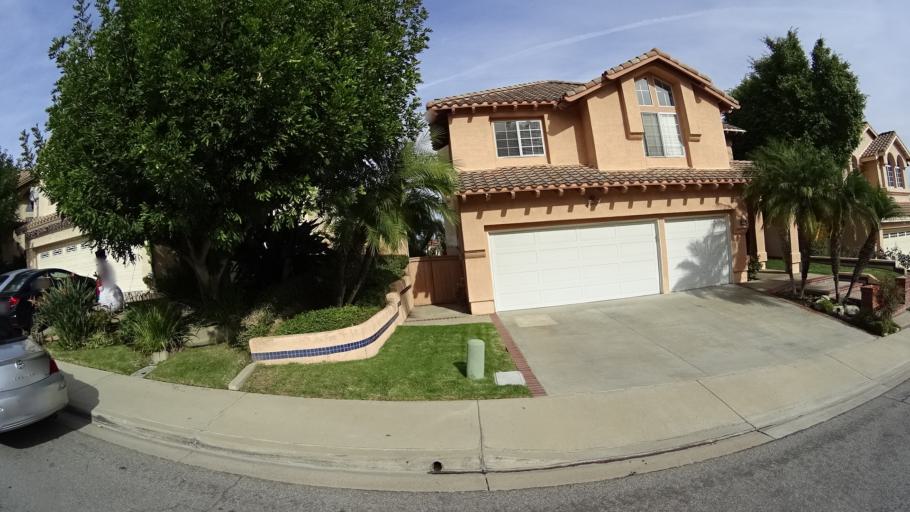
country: US
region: California
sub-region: Orange County
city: Laguna Woods
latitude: 33.5928
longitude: -117.7333
